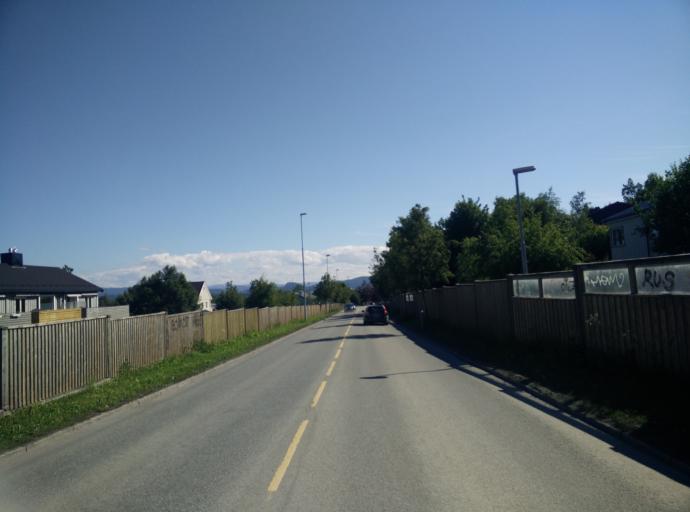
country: NO
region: Sor-Trondelag
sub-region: Trondheim
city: Trondheim
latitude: 63.4011
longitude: 10.3574
